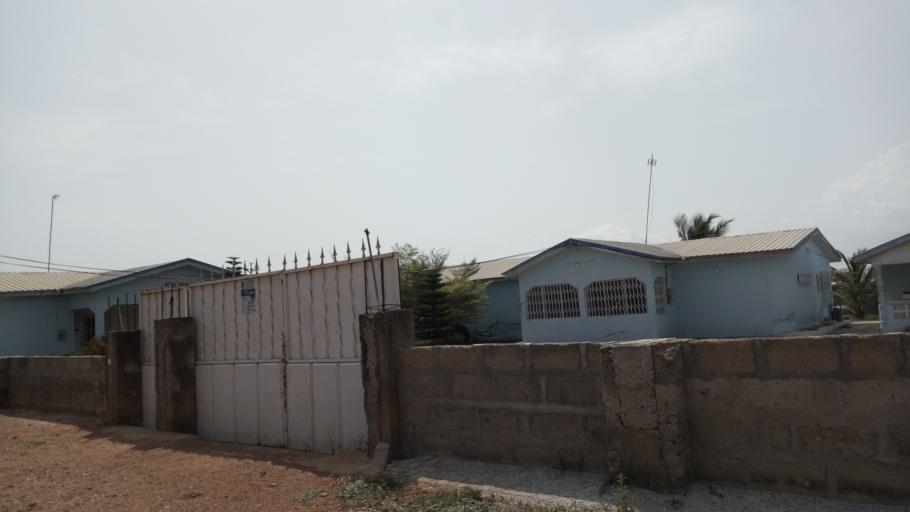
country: GH
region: Central
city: Winneba
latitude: 5.3613
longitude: -0.6381
